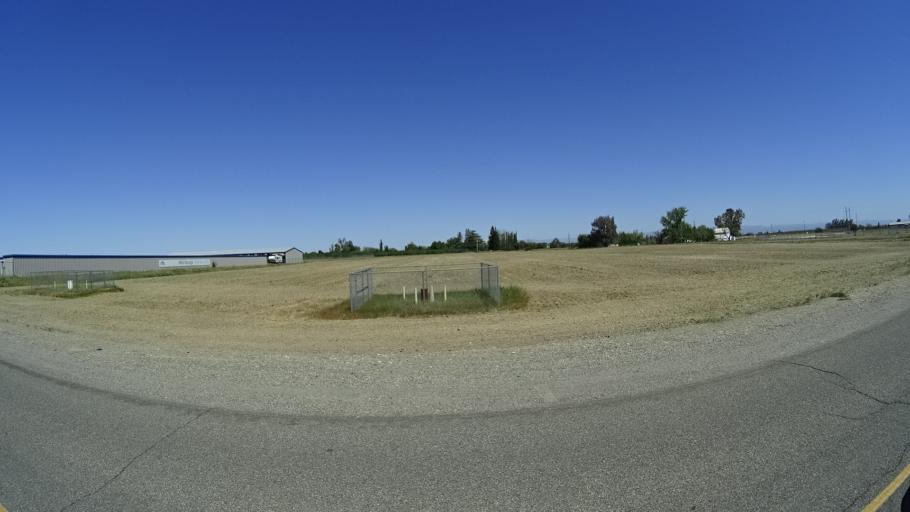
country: US
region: California
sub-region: Glenn County
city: Orland
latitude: 39.7335
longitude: -122.1619
